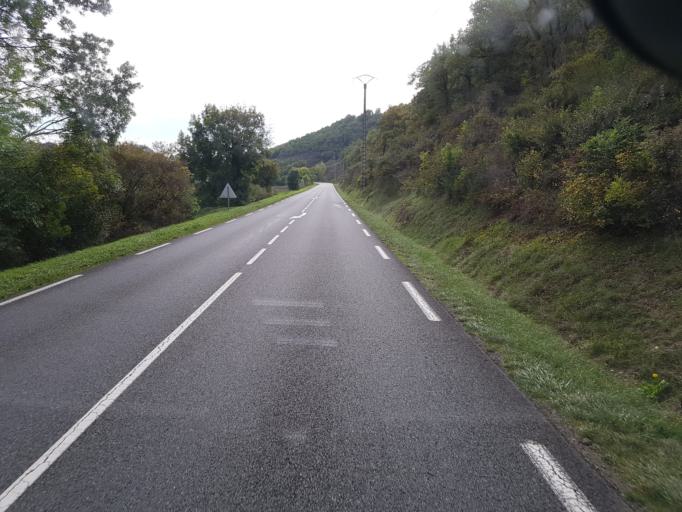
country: FR
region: Midi-Pyrenees
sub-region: Departement de l'Aveyron
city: Saint-Georges-de-Luzencon
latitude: 44.0261
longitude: 2.9648
